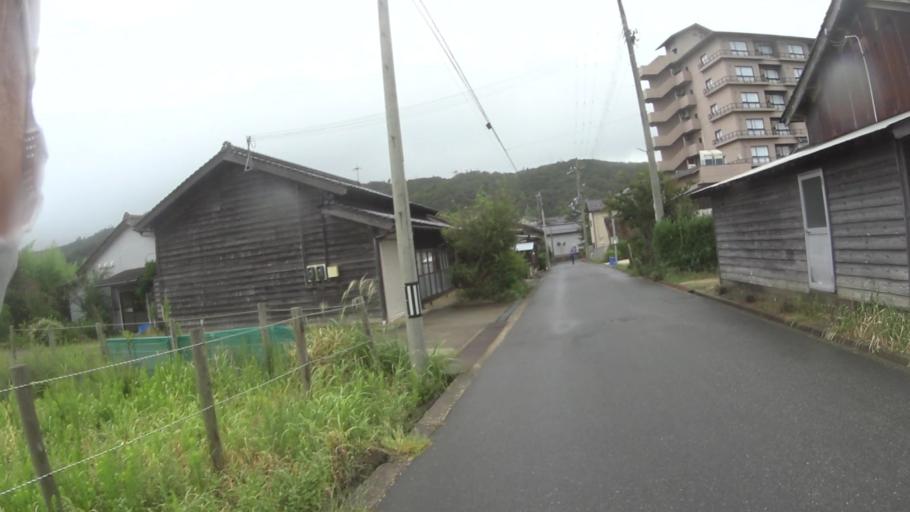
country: JP
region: Hyogo
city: Toyooka
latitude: 35.6602
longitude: 134.9665
